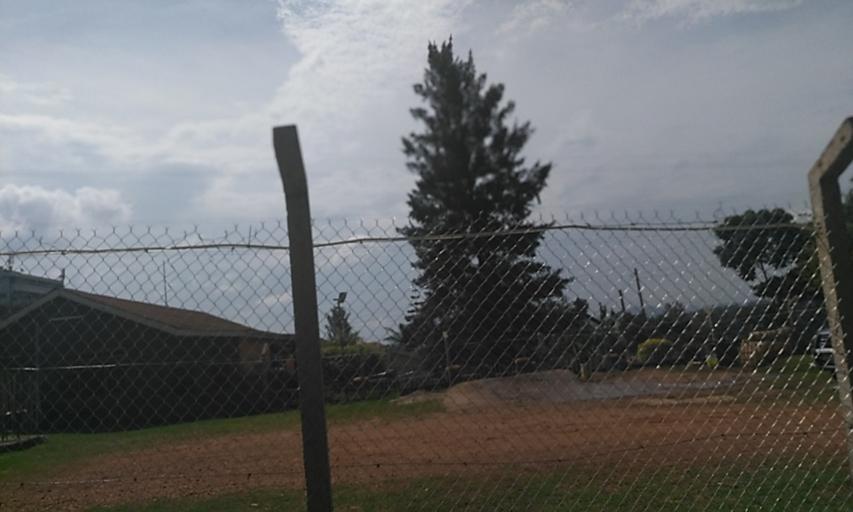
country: UG
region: Central Region
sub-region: Wakiso District
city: Kireka
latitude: 0.3541
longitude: 32.6134
